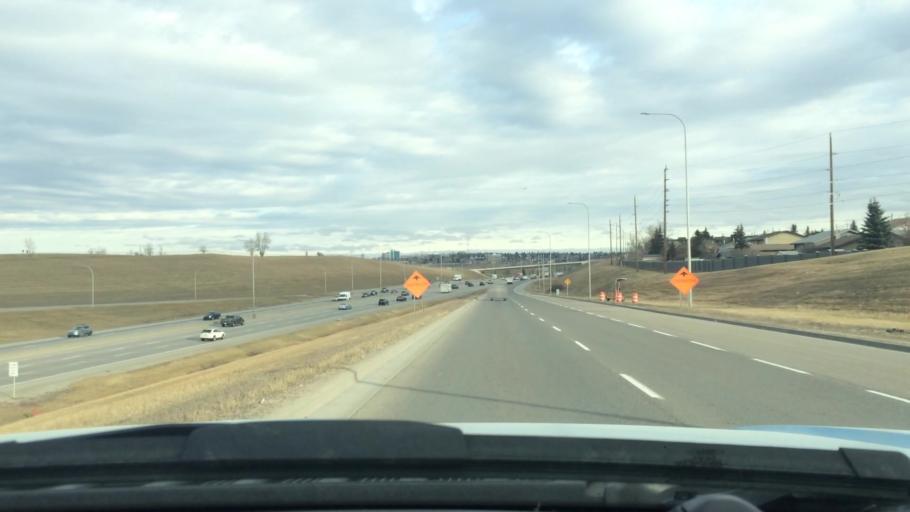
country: CA
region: Alberta
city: Calgary
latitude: 51.0174
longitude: -114.0029
